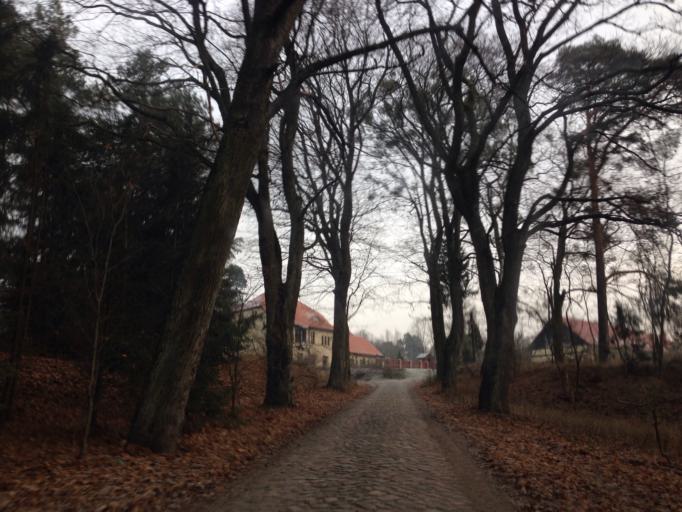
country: PL
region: Kujawsko-Pomorskie
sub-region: Powiat brodnicki
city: Gorzno
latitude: 53.2253
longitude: 19.6540
